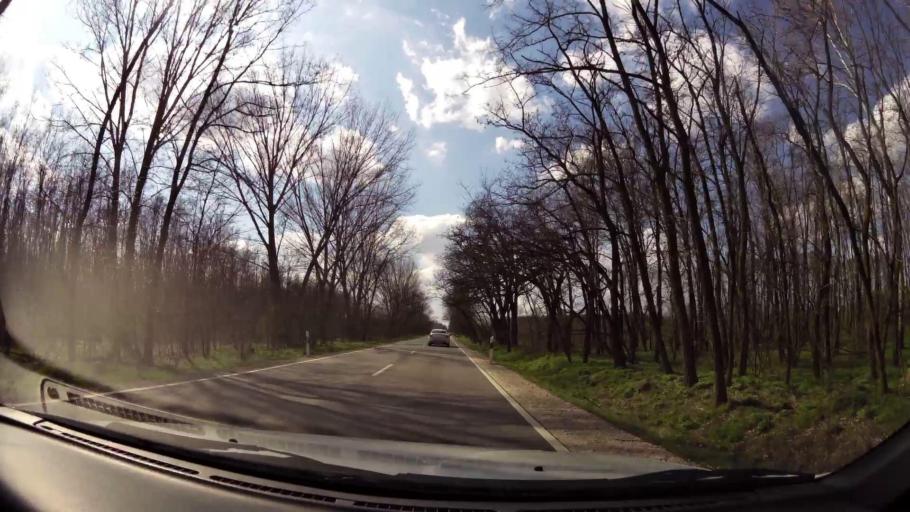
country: HU
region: Pest
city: Forropuszta
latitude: 47.4635
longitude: 19.6360
